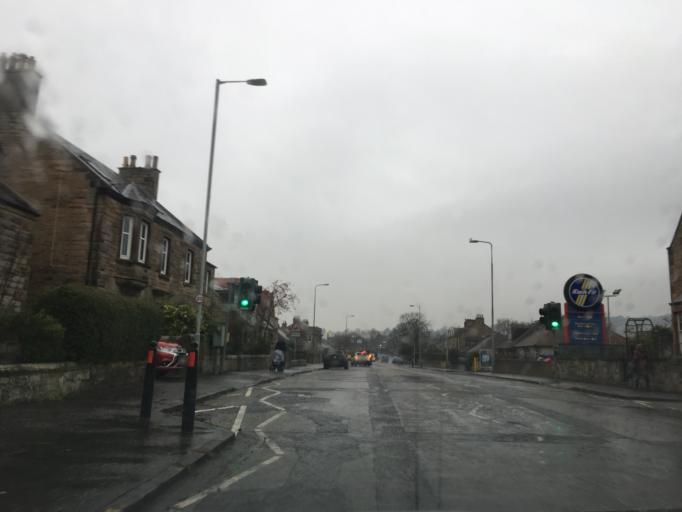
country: GB
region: Scotland
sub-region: Edinburgh
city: Colinton
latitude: 55.9365
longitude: -3.2793
